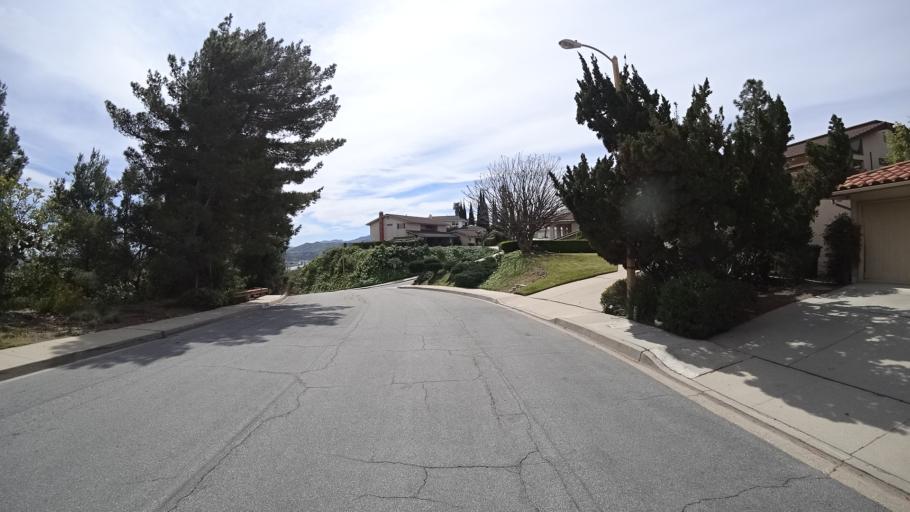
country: US
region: California
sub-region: Ventura County
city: Thousand Oaks
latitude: 34.1541
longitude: -118.8495
